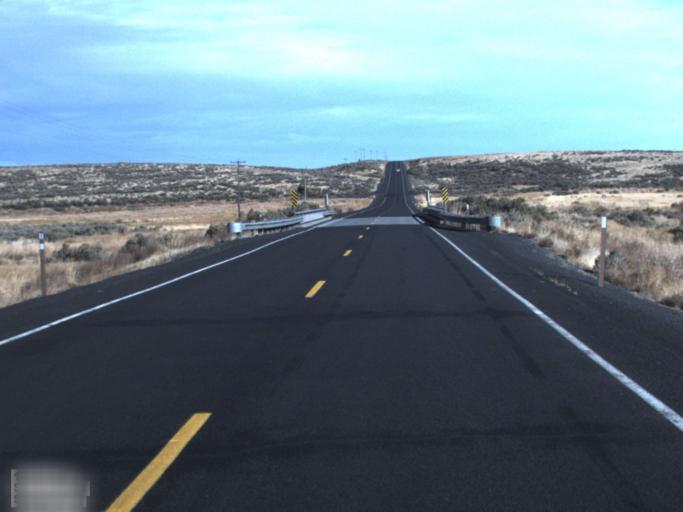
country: US
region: Washington
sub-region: Adams County
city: Ritzville
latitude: 47.2255
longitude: -118.6863
